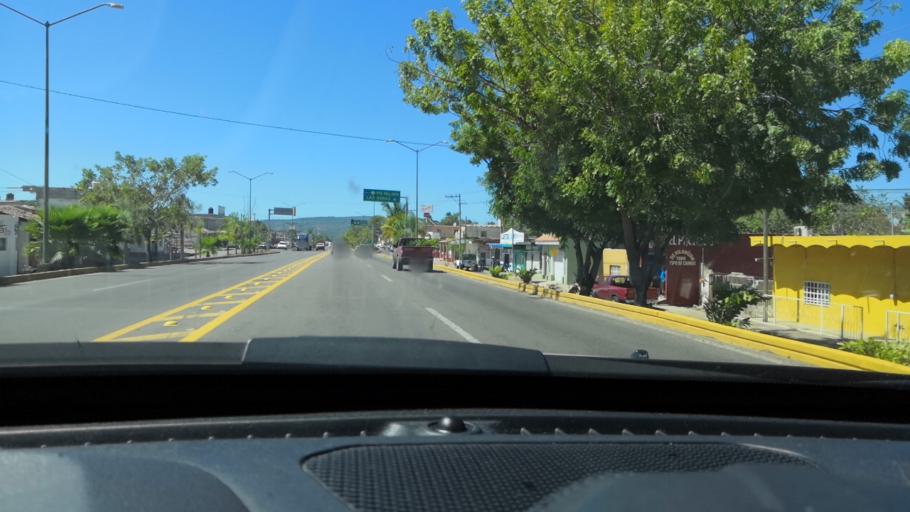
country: MX
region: Nayarit
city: Las Varas
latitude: 21.1838
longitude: -105.1293
